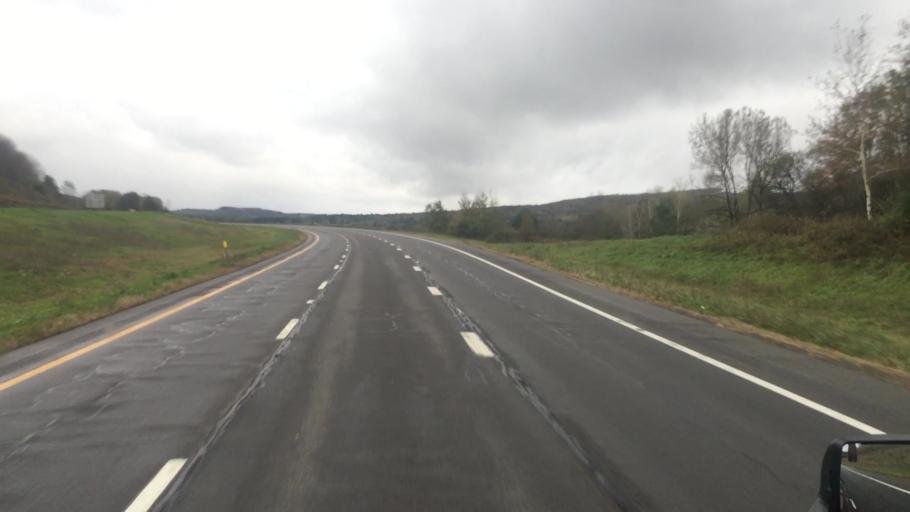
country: US
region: New York
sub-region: Chenango County
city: Greene
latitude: 42.1938
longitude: -75.6579
